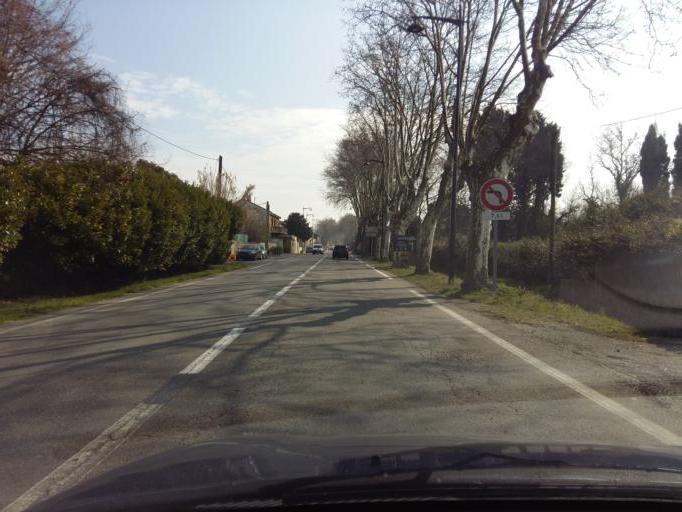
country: FR
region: Provence-Alpes-Cote d'Azur
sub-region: Departement des Bouches-du-Rhone
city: Molleges
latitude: 43.8087
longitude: 4.9933
